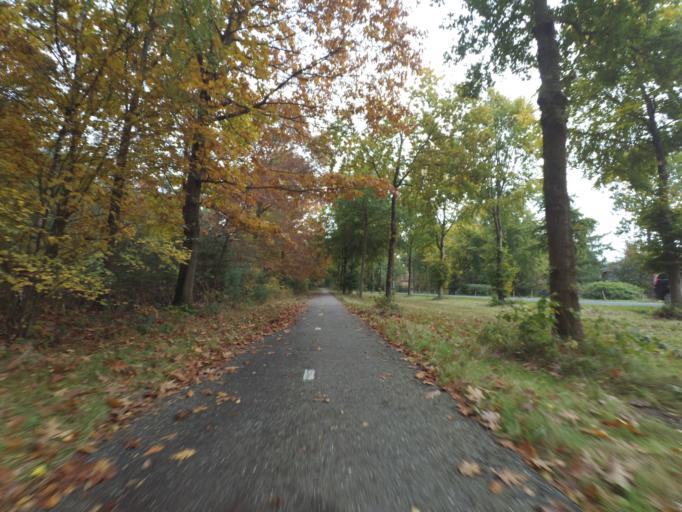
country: NL
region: Gelderland
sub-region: Gemeente Ermelo
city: Ermelo
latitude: 52.3032
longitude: 5.6555
